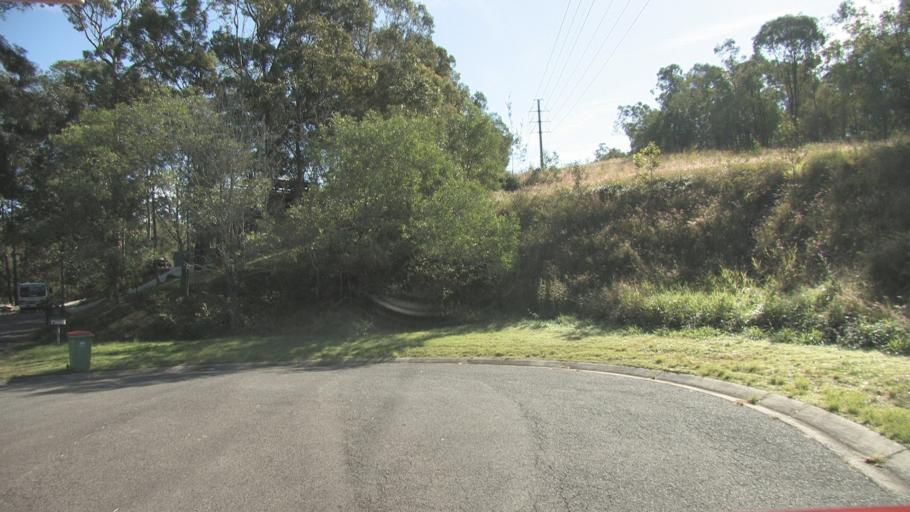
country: AU
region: Queensland
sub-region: Logan
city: Windaroo
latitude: -27.7333
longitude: 153.1916
